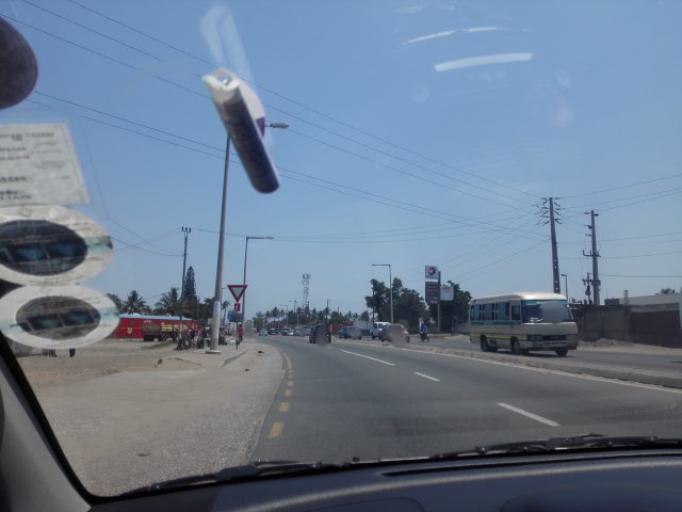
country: MZ
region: Maputo City
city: Maputo
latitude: -25.9047
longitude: 32.5656
